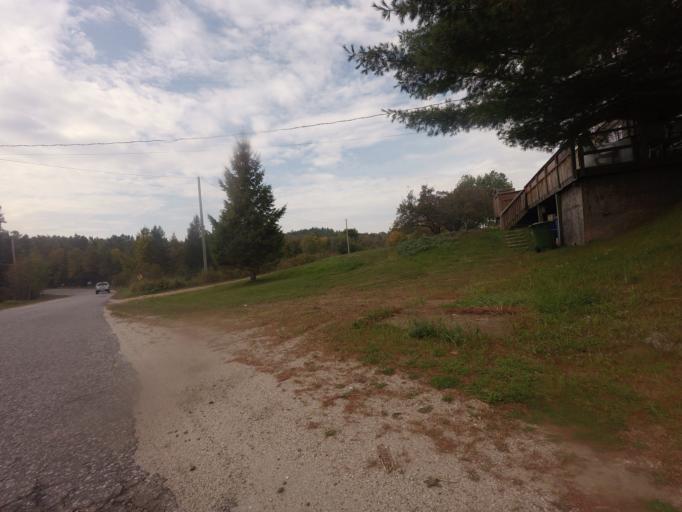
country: CA
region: Quebec
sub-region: Outaouais
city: Wakefield
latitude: 45.9721
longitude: -75.9364
